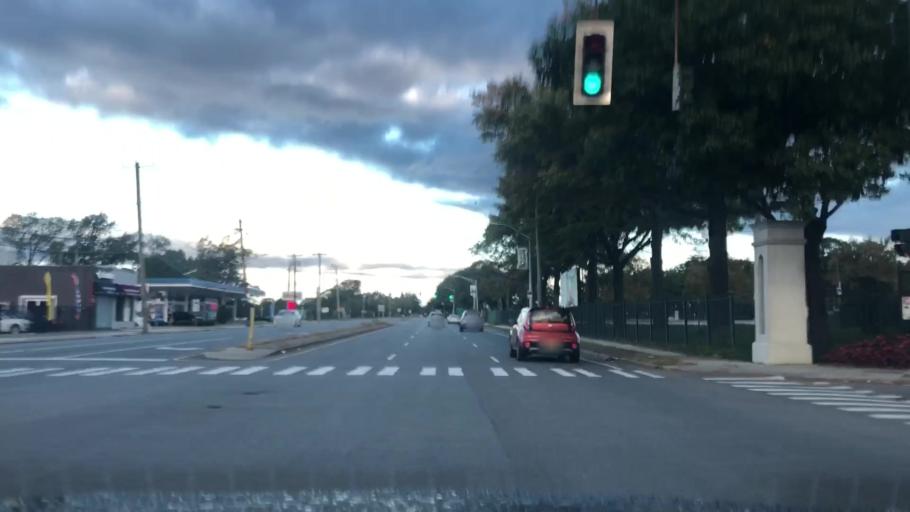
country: US
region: New York
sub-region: Nassau County
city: Elmont
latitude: 40.7092
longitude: -73.7215
